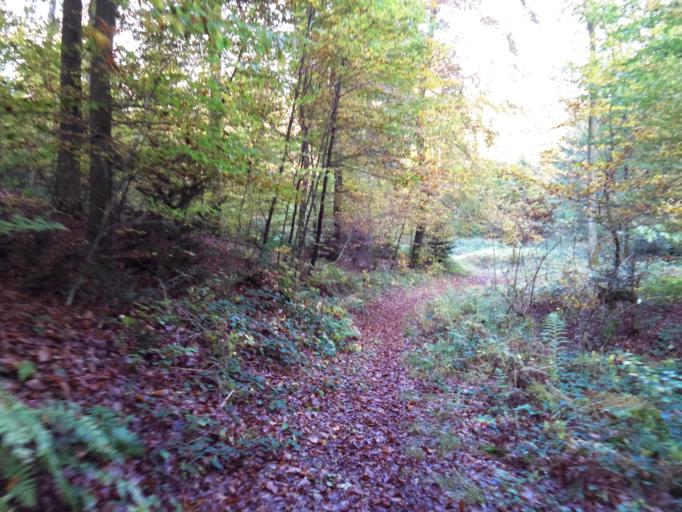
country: DE
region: Rheinland-Pfalz
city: Frankenstein
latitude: 49.4476
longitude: 8.0079
